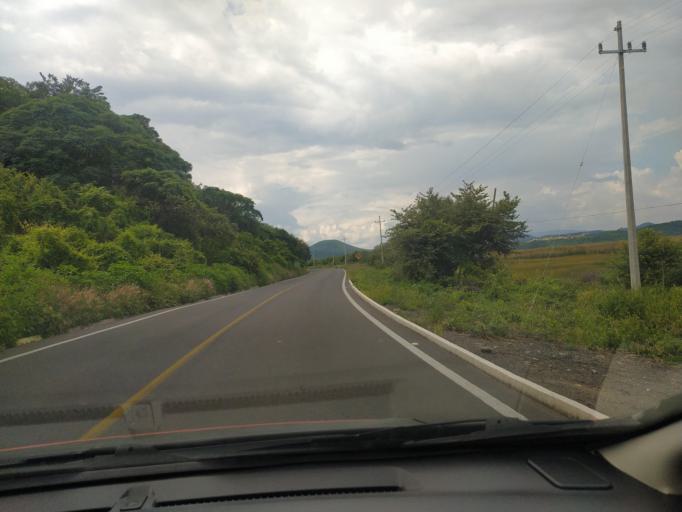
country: MX
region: Jalisco
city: Villa Corona
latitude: 20.3877
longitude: -103.6740
